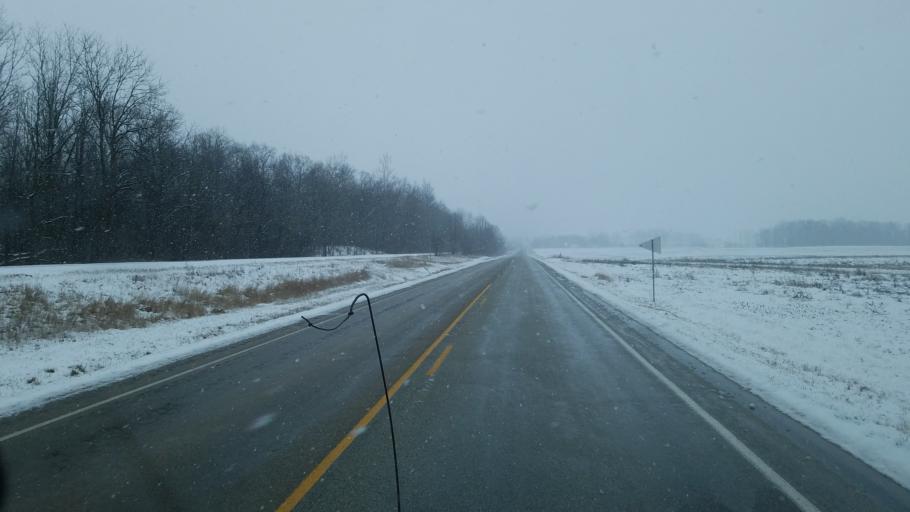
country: US
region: Indiana
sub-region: Wayne County
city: Hagerstown
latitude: 39.9728
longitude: -85.0459
